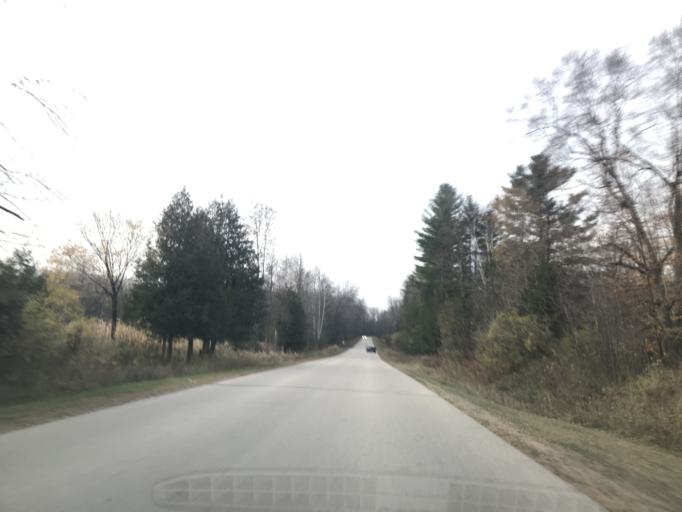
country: US
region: Wisconsin
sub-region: Marinette County
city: Peshtigo
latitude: 45.0666
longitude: -87.7994
